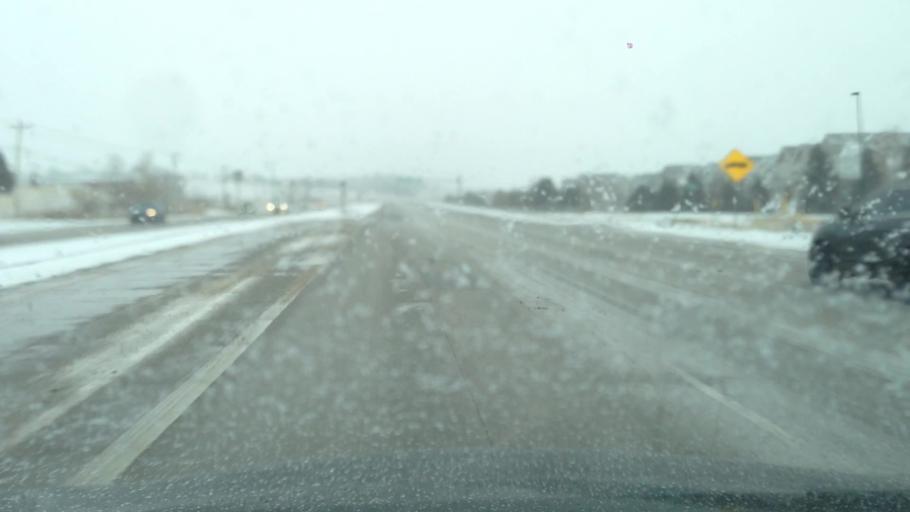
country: US
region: Colorado
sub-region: Arapahoe County
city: Dove Valley
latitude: 39.5863
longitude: -104.7972
